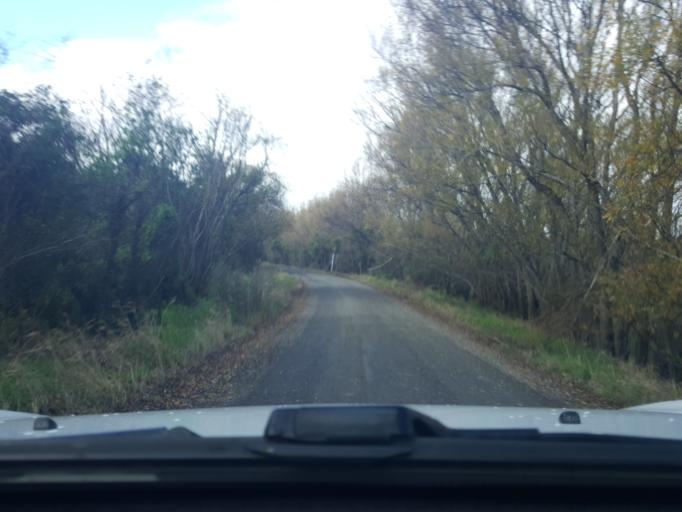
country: NZ
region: Waikato
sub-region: Waikato District
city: Te Kauwhata
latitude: -37.4103
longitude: 175.0588
